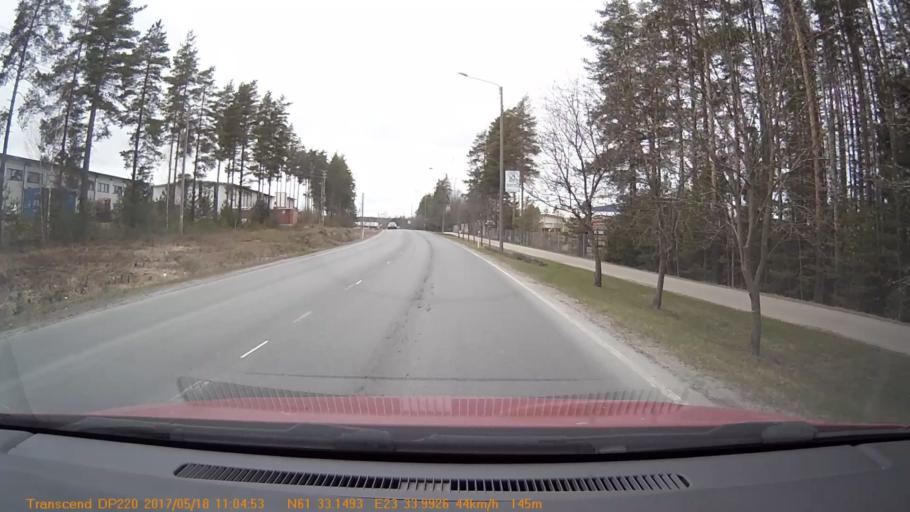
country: FI
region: Pirkanmaa
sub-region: Tampere
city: Yloejaervi
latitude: 61.5523
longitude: 23.5670
